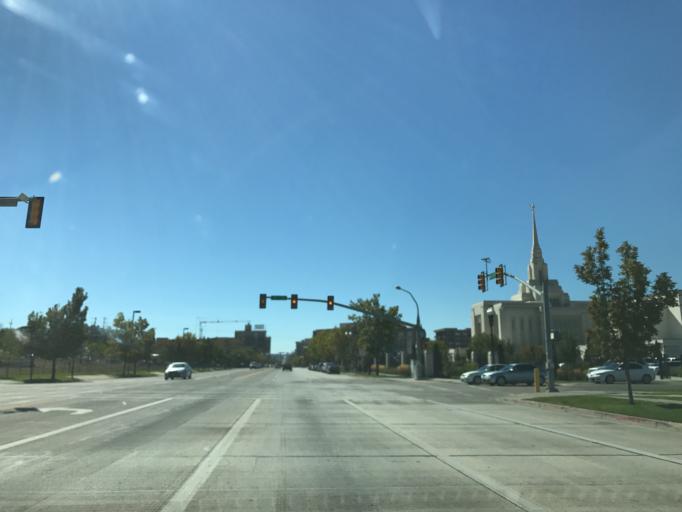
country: US
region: Utah
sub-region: Weber County
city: Ogden
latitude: 41.2295
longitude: -111.9704
